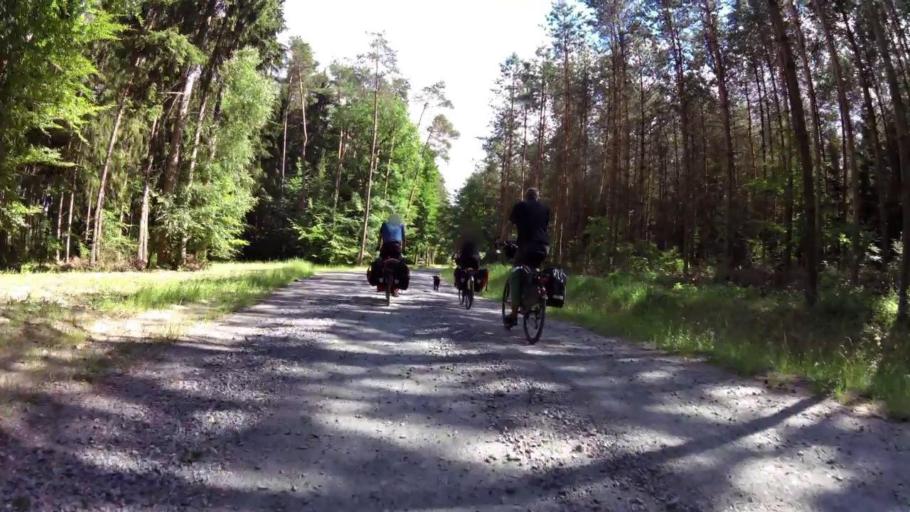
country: PL
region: West Pomeranian Voivodeship
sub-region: Powiat lobeski
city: Lobez
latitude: 53.6827
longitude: 15.5500
